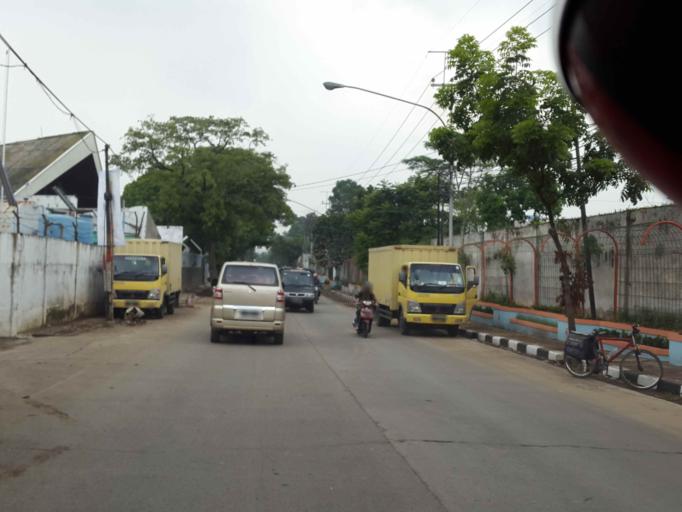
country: ID
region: West Java
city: Cimahi
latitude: -6.8989
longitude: 107.5521
